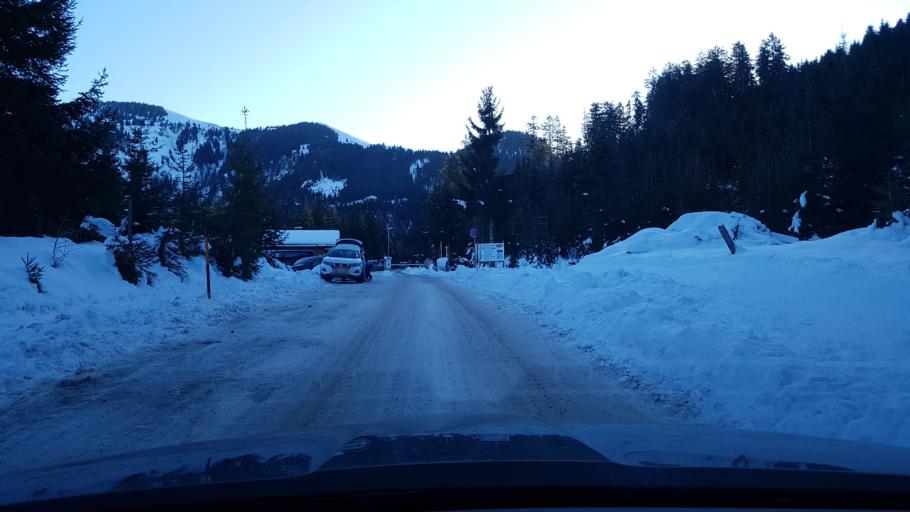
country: AT
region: Salzburg
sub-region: Politischer Bezirk Hallein
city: Scheffau am Tennengebirge
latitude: 47.6446
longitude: 13.2408
